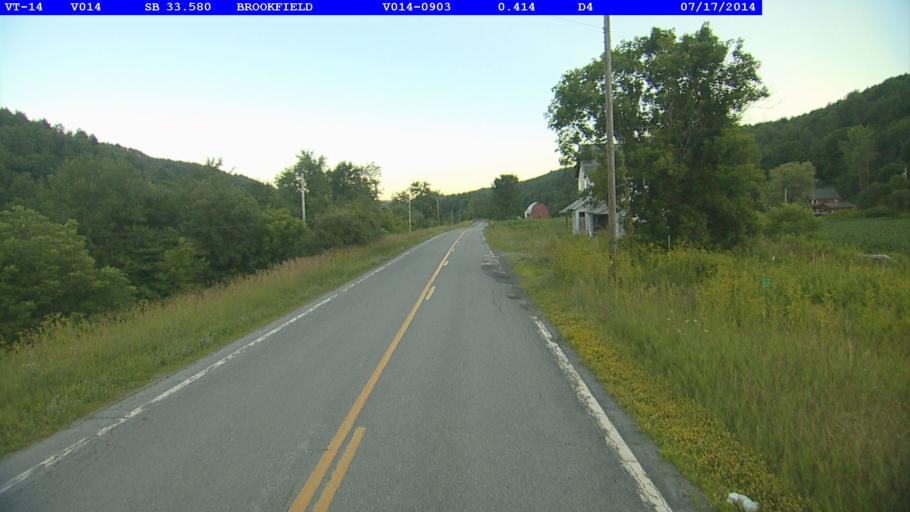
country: US
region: Vermont
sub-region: Orange County
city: Chelsea
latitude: 43.9850
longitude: -72.5572
